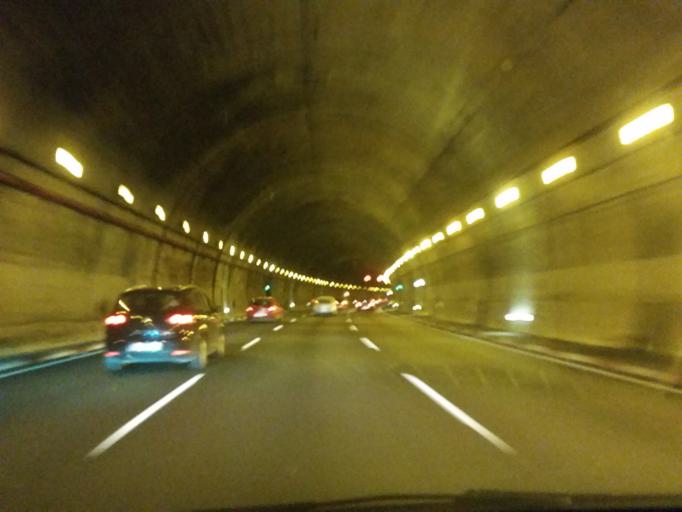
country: ES
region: Andalusia
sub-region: Provincia de Malaga
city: Malaga
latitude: 36.7404
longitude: -4.3845
